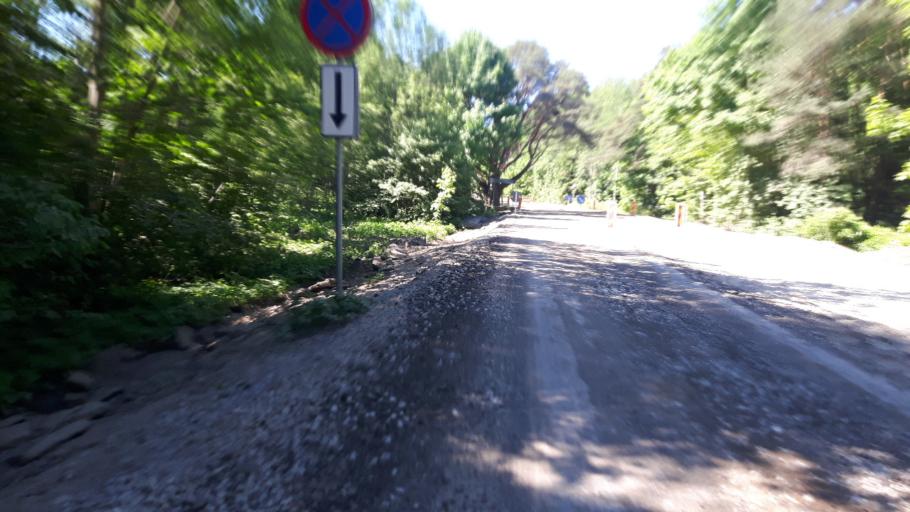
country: EE
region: Ida-Virumaa
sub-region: Narva-Joesuu linn
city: Narva-Joesuu
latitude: 59.4159
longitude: 27.9636
